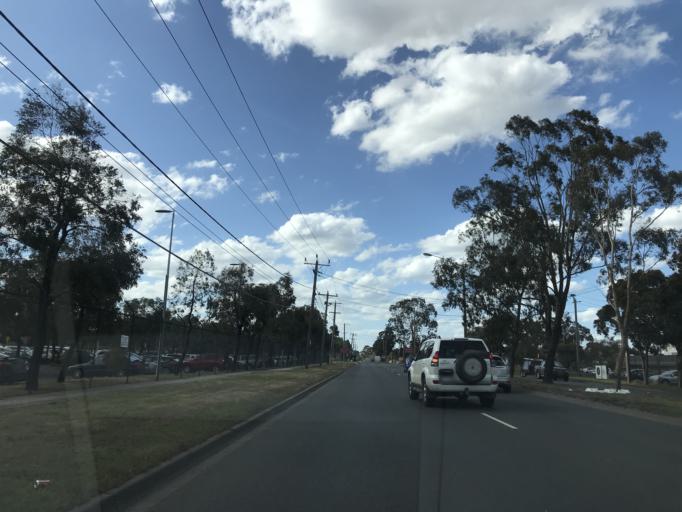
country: AU
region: Victoria
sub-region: Brimbank
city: Sunshine West
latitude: -37.8093
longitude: 144.8180
